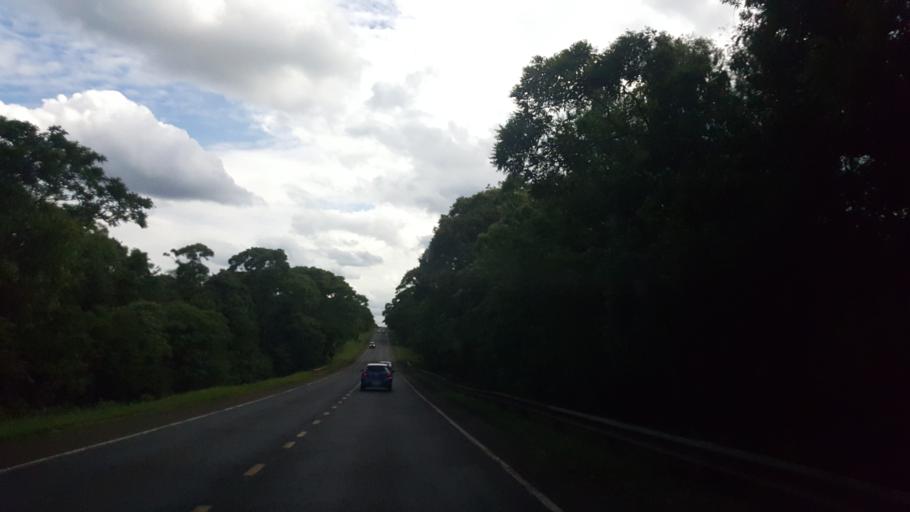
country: AR
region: Misiones
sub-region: Departamento de Iguazu
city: Puerto Iguazu
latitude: -25.7049
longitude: -54.5152
